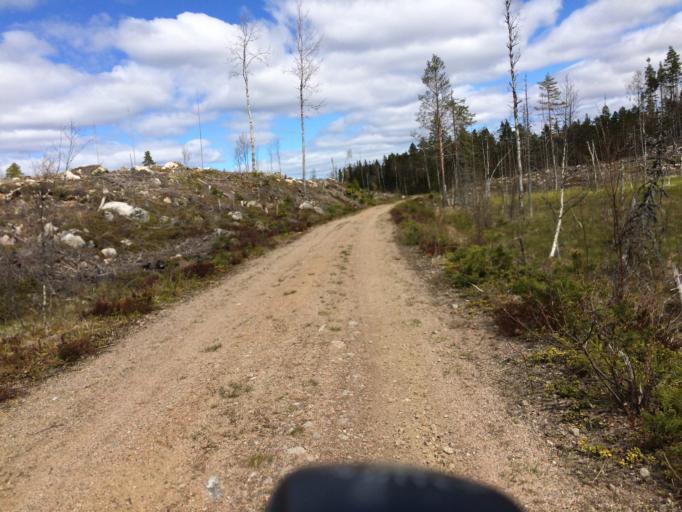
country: SE
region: OErebro
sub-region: Hallefors Kommun
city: Haellefors
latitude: 60.0526
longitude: 14.5236
